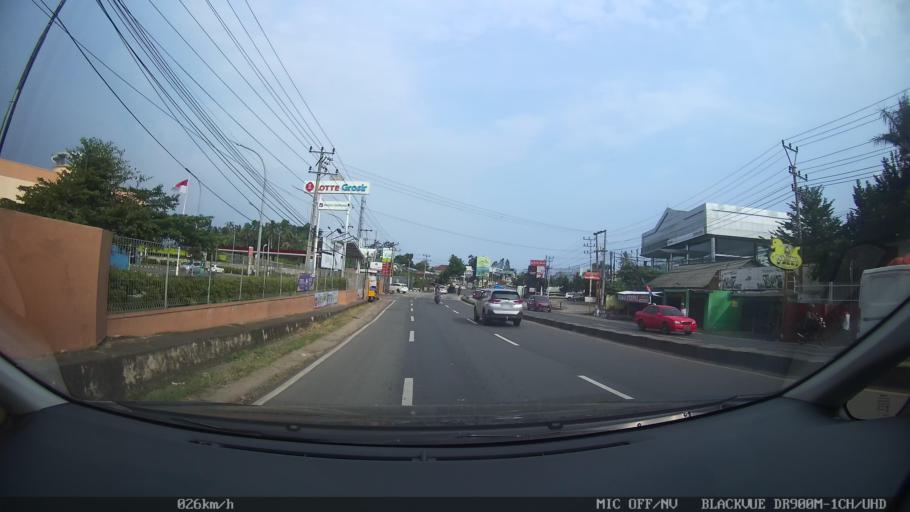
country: ID
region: Lampung
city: Kedaton
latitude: -5.3542
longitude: 105.2197
